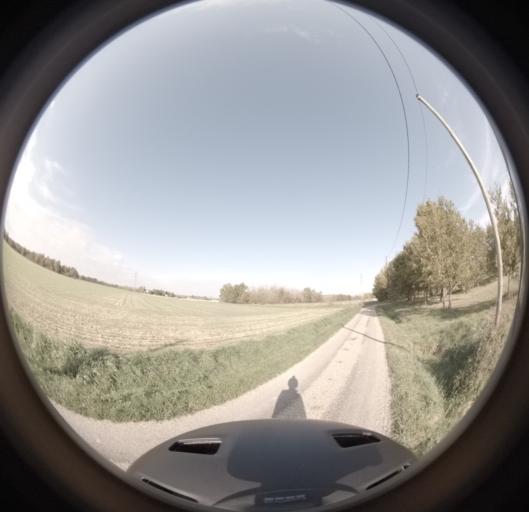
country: FR
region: Midi-Pyrenees
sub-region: Departement du Tarn-et-Garonne
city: Montbeton
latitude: 43.9923
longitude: 1.2752
